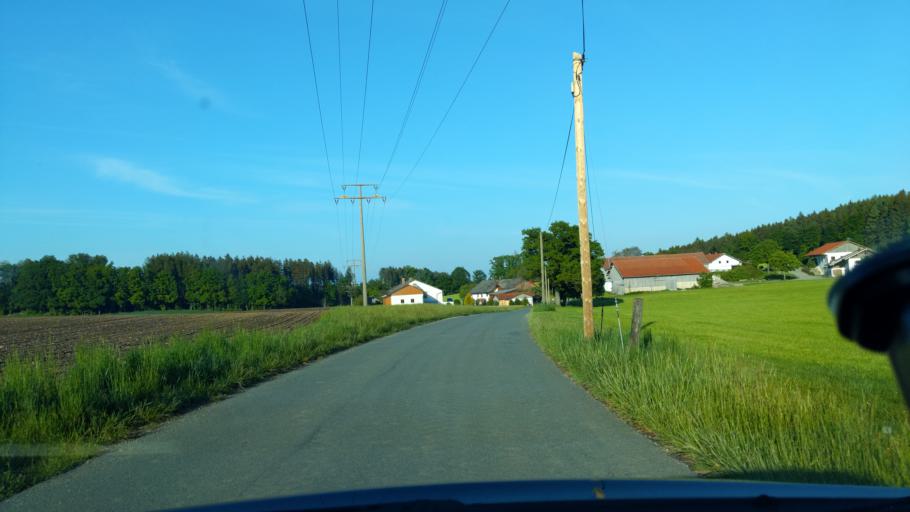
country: DE
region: Bavaria
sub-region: Upper Bavaria
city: Ebersberg
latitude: 48.0706
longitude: 11.9914
